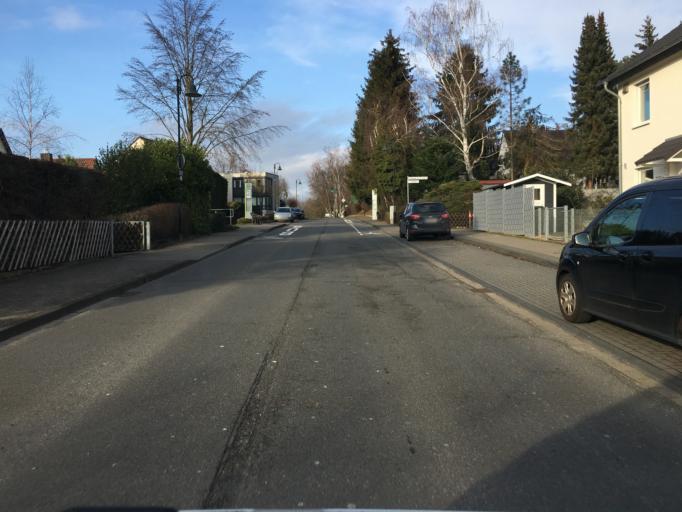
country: DE
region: North Rhine-Westphalia
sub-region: Regierungsbezirk Koln
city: Rosrath
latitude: 50.9211
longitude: 7.1746
